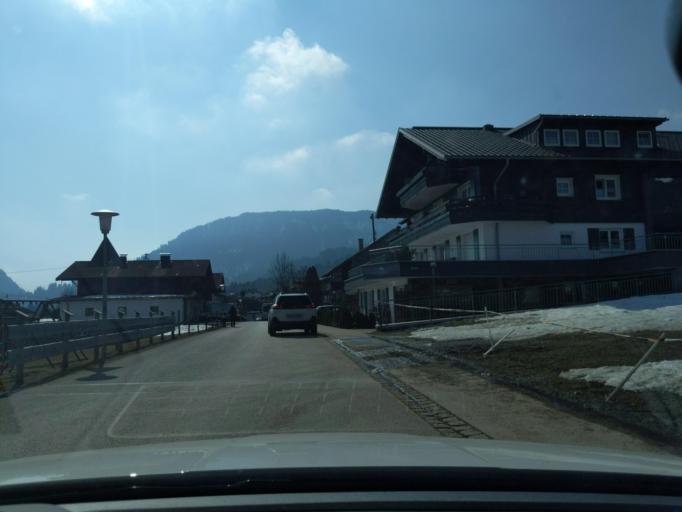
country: DE
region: Bavaria
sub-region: Swabia
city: Obermaiselstein
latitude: 47.4564
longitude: 10.2317
